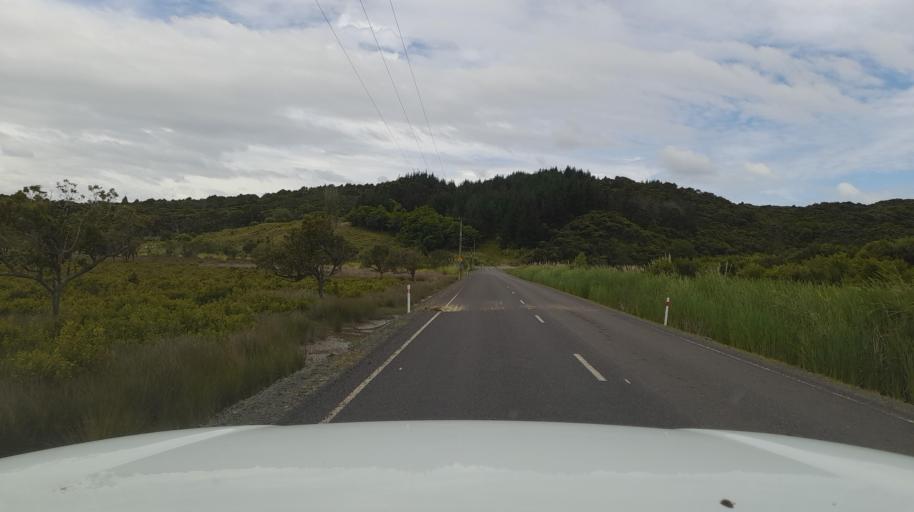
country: NZ
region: Northland
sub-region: Far North District
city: Kaitaia
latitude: -35.4061
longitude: 173.3824
